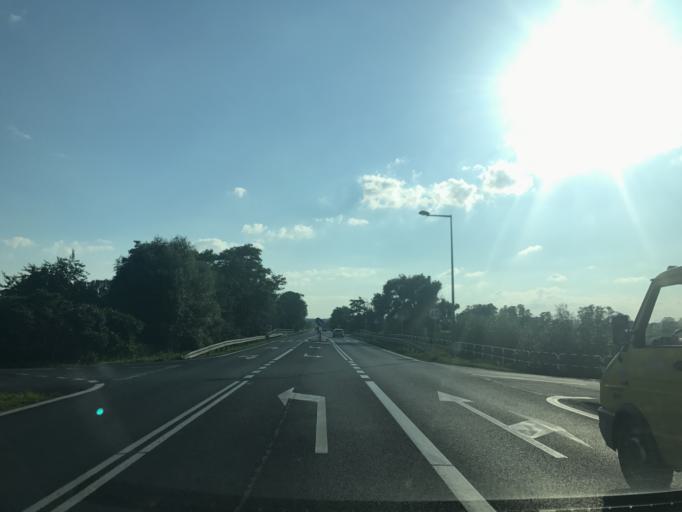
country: PL
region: Greater Poland Voivodeship
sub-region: Powiat kolski
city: Koscielec
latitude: 52.1823
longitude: 18.6058
